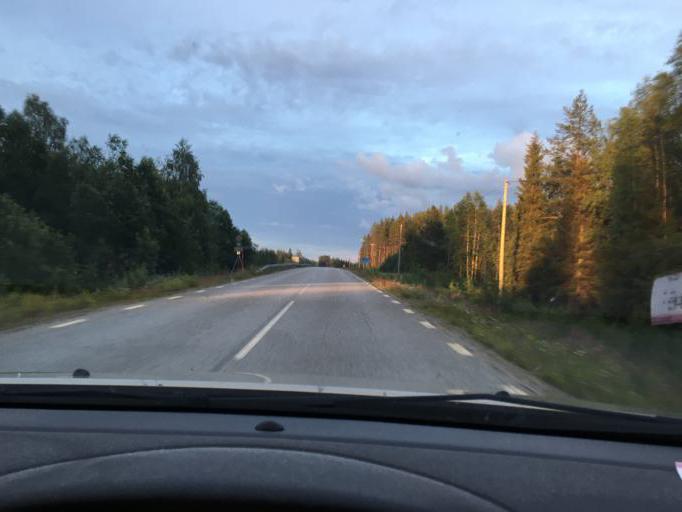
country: SE
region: Norrbotten
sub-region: Lulea Kommun
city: Ranea
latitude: 66.0426
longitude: 22.2945
